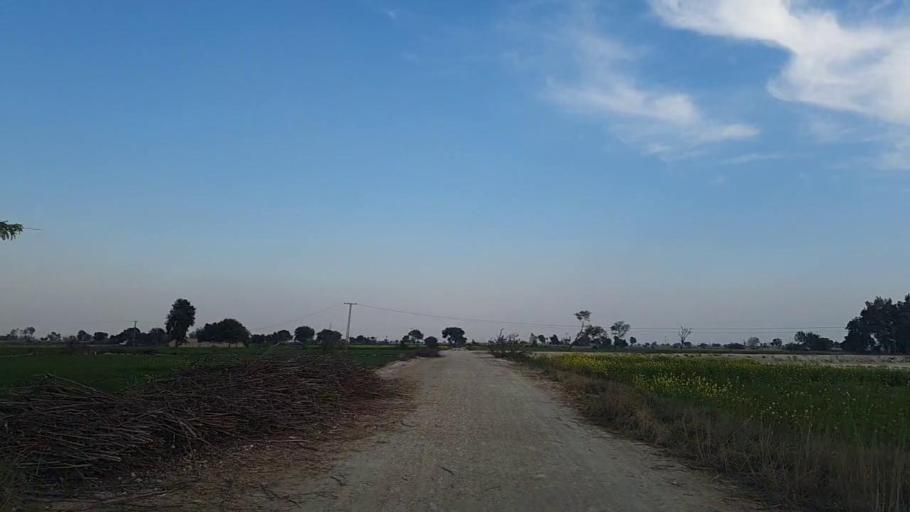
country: PK
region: Sindh
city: Bandhi
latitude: 26.5573
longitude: 68.2798
